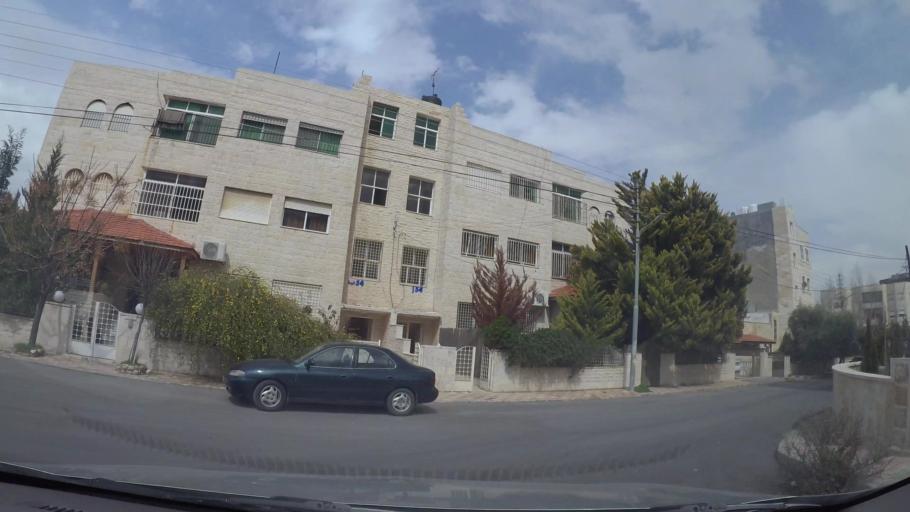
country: JO
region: Amman
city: Umm as Summaq
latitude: 31.8990
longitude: 35.8350
